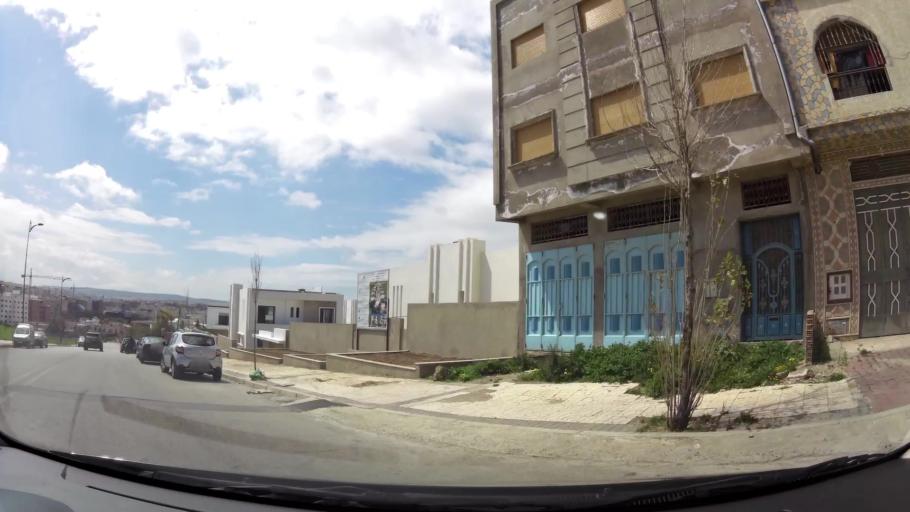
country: MA
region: Tanger-Tetouan
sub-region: Tanger-Assilah
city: Tangier
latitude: 35.7676
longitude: -5.8393
